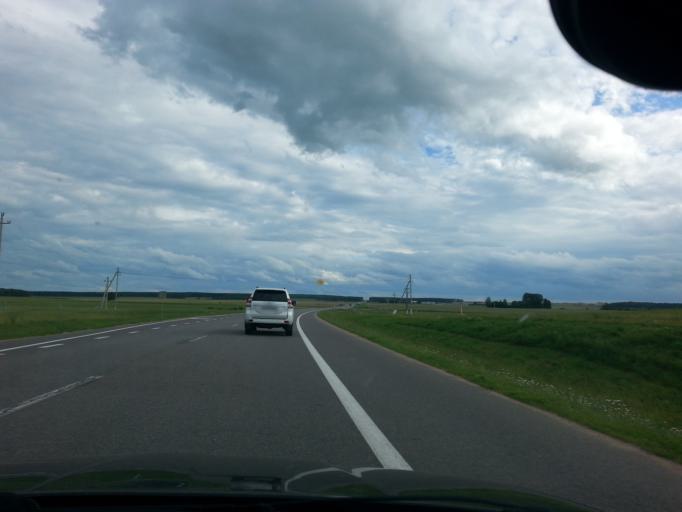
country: BY
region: Grodnenskaya
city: Astravyets
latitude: 54.7370
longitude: 26.0874
